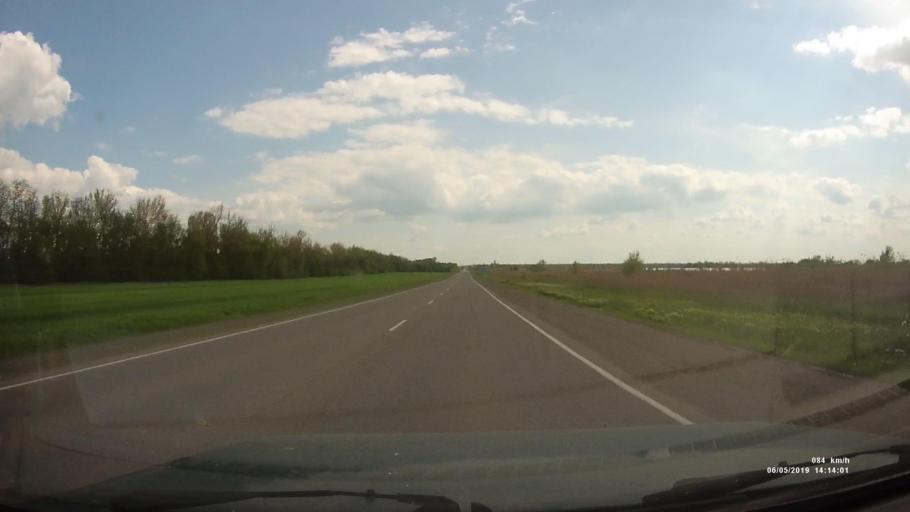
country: RU
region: Rostov
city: Kamenolomni
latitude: 47.6536
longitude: 40.2950
